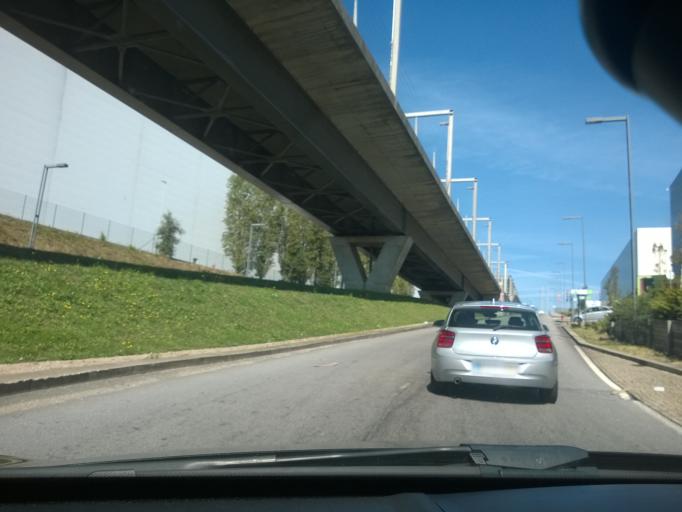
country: PT
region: Porto
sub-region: Maia
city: Maia
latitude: 41.2427
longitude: -8.6280
